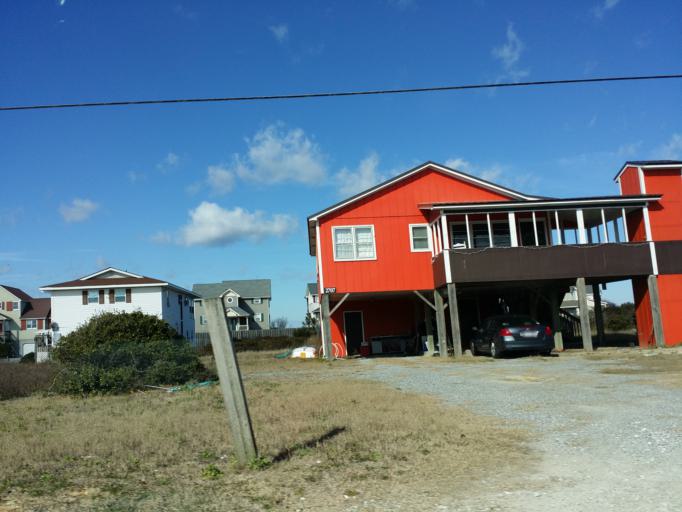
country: US
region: North Carolina
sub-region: Pender County
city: Surf City
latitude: 34.4568
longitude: -77.4939
